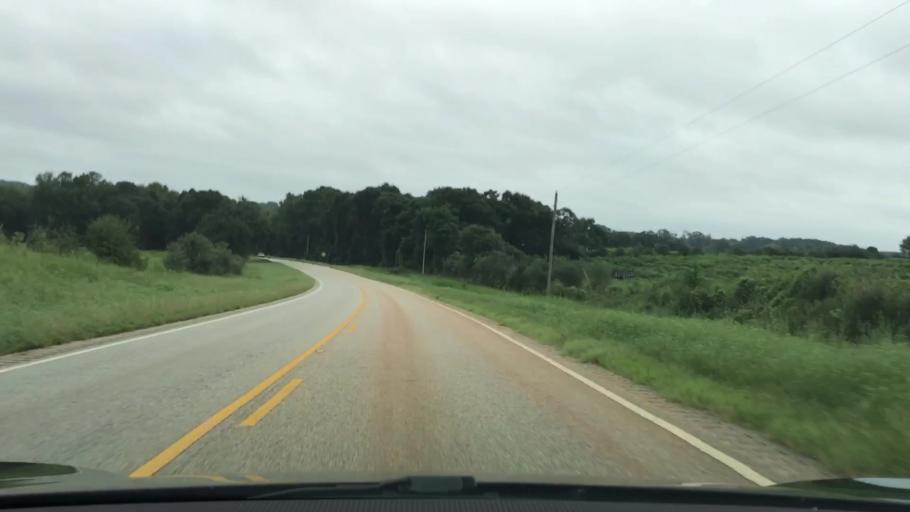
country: US
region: Alabama
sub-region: Covington County
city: Opp
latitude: 31.2920
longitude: -86.1443
